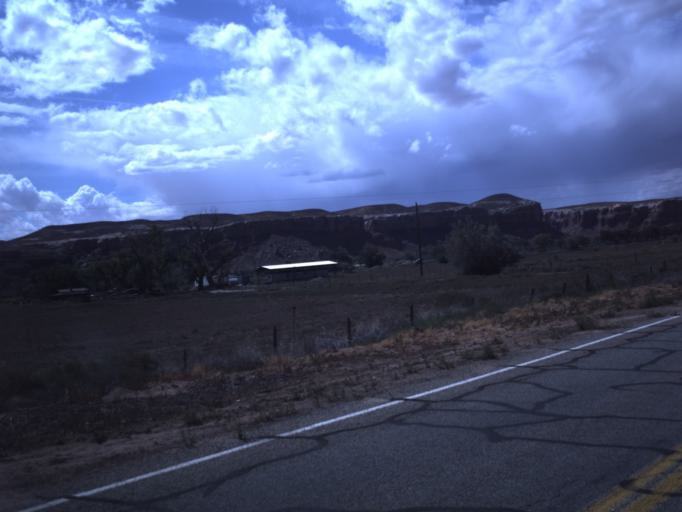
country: US
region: Utah
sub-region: San Juan County
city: Blanding
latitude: 37.2852
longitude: -109.5252
